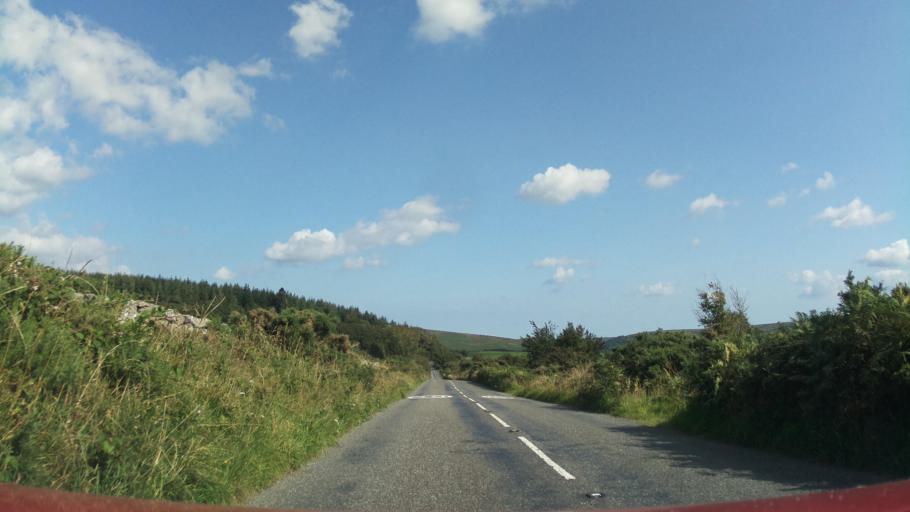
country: GB
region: England
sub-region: Devon
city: Buckfastleigh
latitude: 50.5477
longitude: -3.8970
